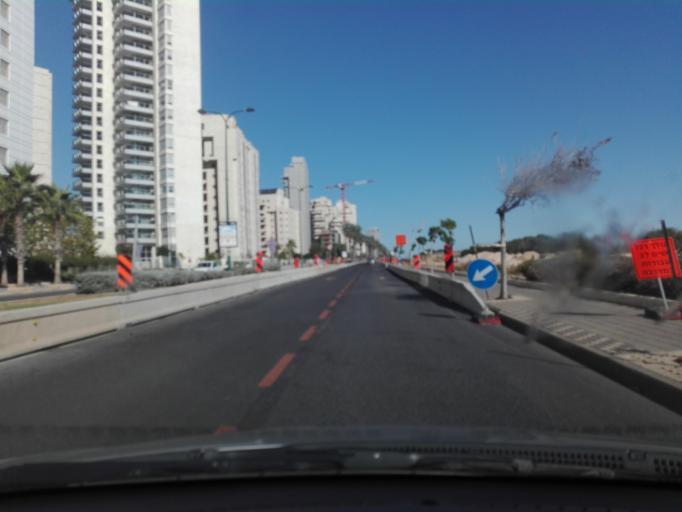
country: IL
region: Central District
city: Netanya
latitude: 32.3045
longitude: 34.8461
